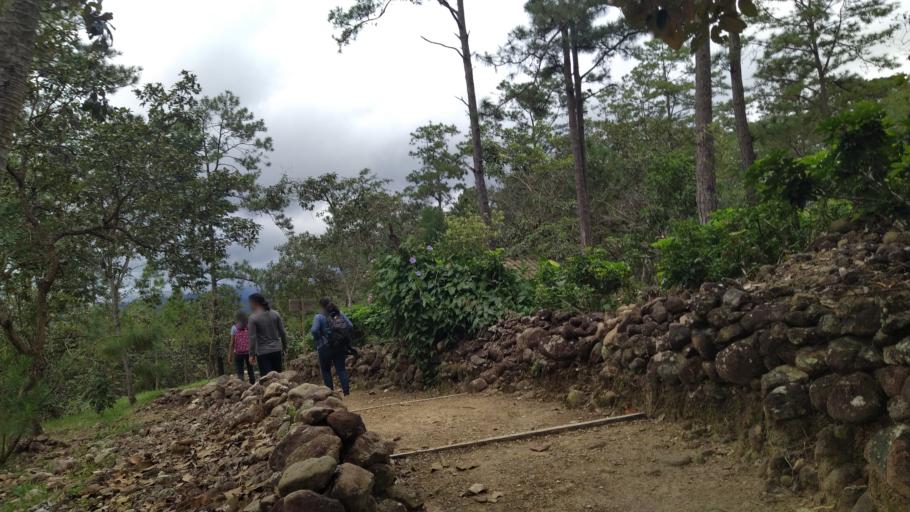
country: GT
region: Chiquimula
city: Esquipulas
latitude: 14.5565
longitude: -89.3199
